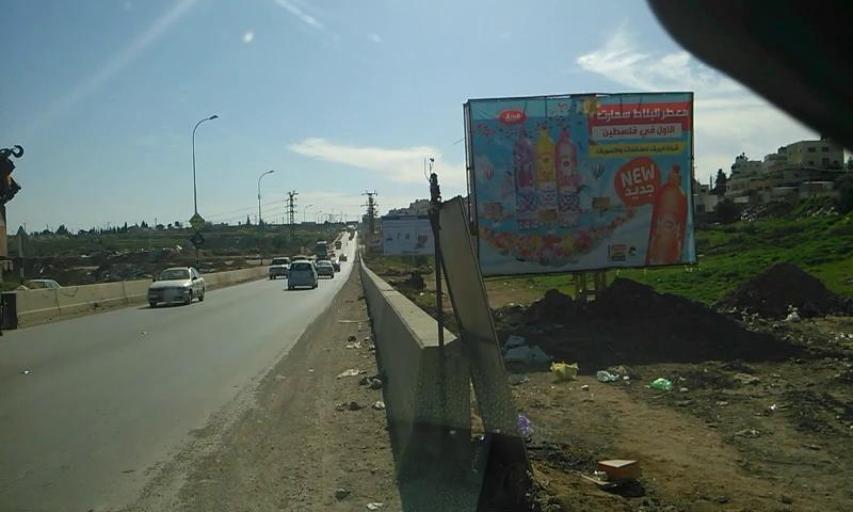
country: PS
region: West Bank
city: Ar Ram wa Dahiyat al Barid
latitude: 31.8591
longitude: 35.2332
